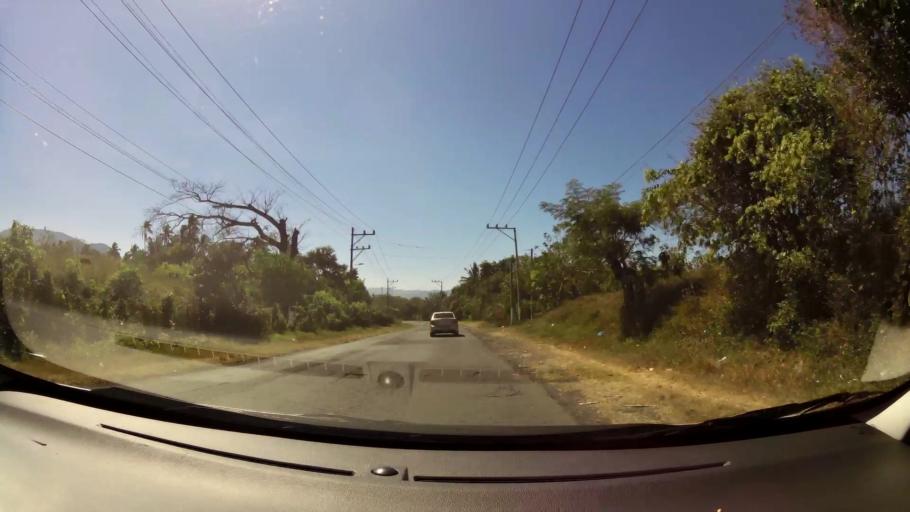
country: SV
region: La Libertad
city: San Juan Opico
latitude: 13.8171
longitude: -89.3566
